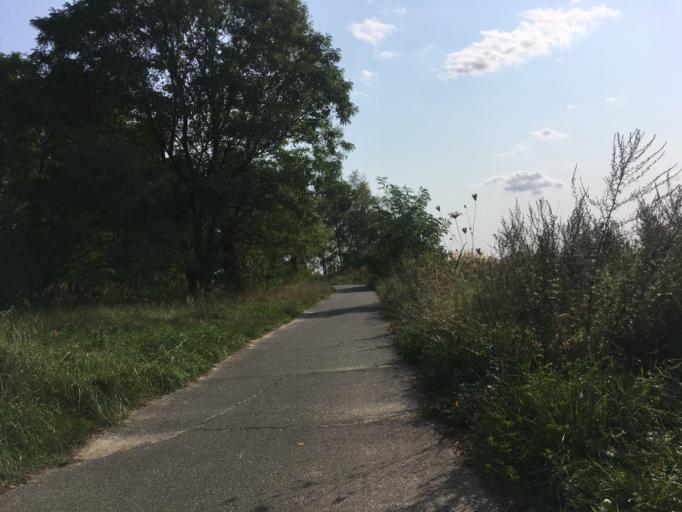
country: DE
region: Berlin
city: Frohnau
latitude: 52.6529
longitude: 13.2813
